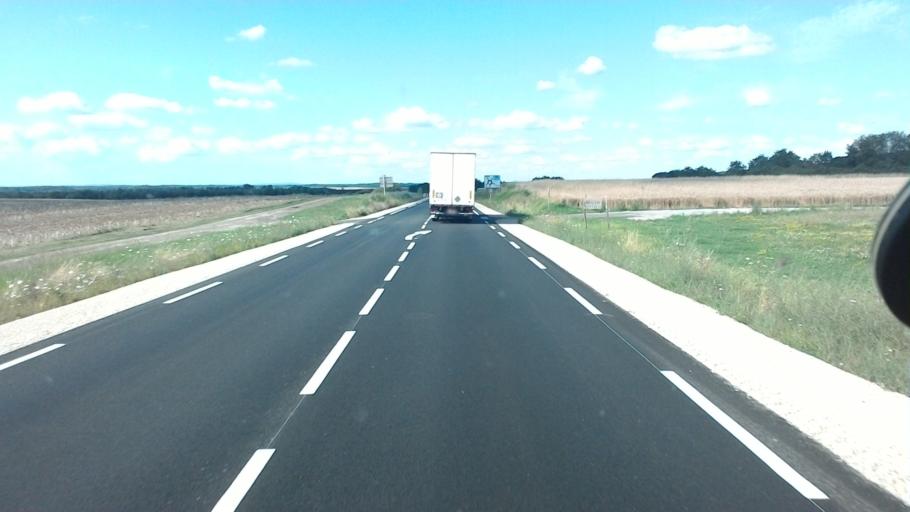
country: FR
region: Franche-Comte
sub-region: Departement de la Haute-Saone
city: Marnay
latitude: 47.3381
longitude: 5.6981
